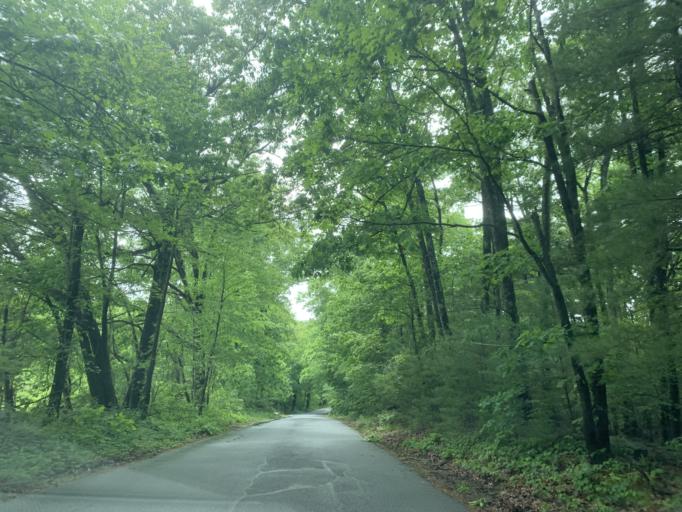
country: US
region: Massachusetts
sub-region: Worcester County
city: Grafton
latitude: 42.2012
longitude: -71.6413
